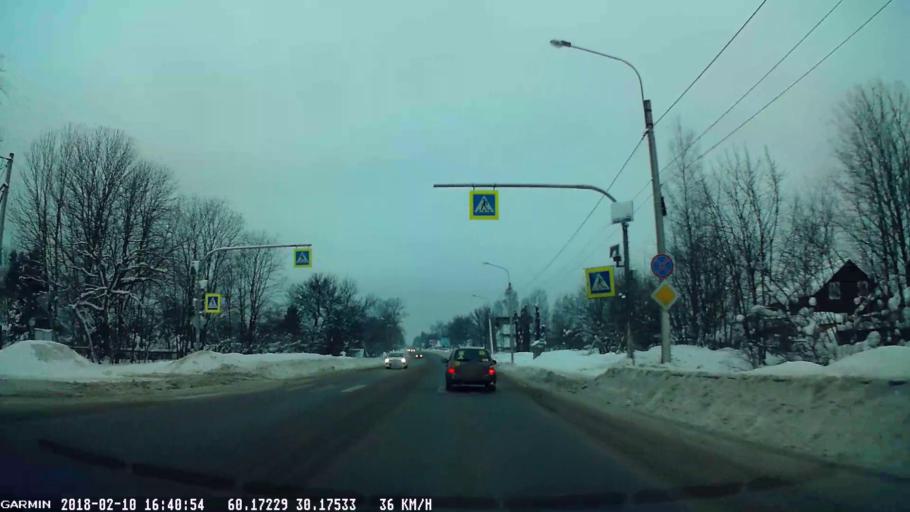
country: RU
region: Leningrad
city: Sertolovo
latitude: 60.1623
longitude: 30.1833
